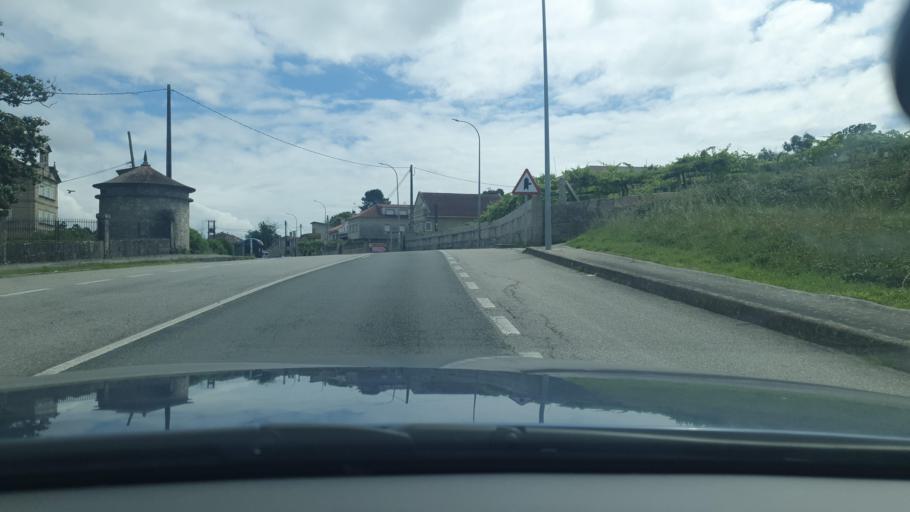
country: ES
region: Galicia
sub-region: Provincia de Pontevedra
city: Cambados
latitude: 42.4906
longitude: -8.8029
